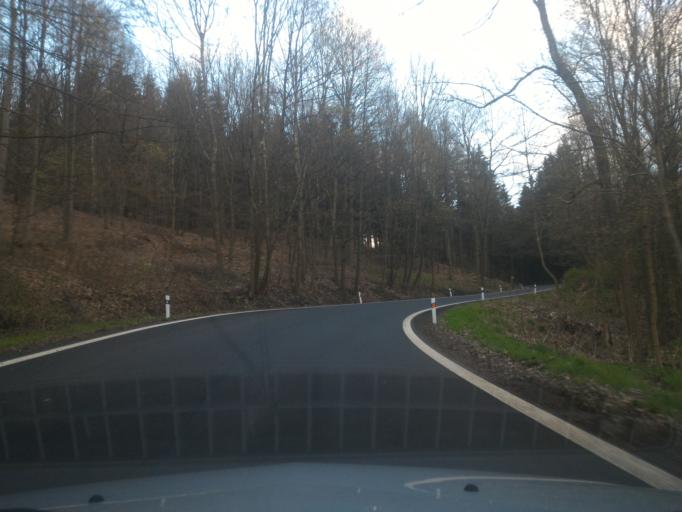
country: CZ
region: Ustecky
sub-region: Okres Decin
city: Krasna Lipa
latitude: 50.9144
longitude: 14.5289
